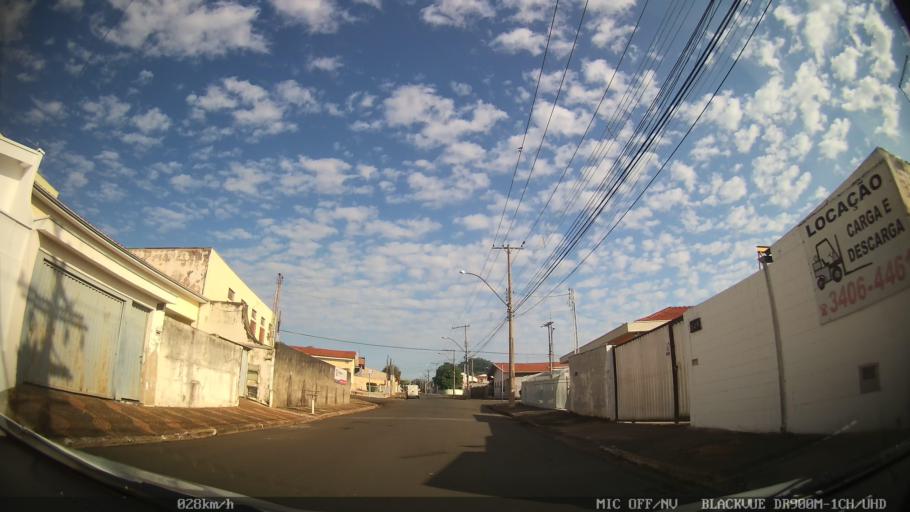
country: BR
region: Sao Paulo
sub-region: Americana
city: Americana
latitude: -22.7439
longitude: -47.3469
